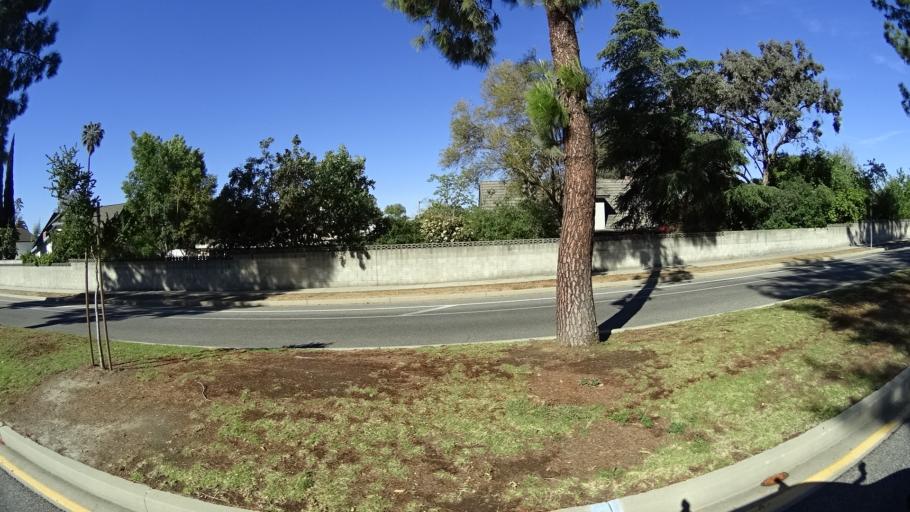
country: US
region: California
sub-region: Ventura County
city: Thousand Oaks
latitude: 34.2228
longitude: -118.8573
